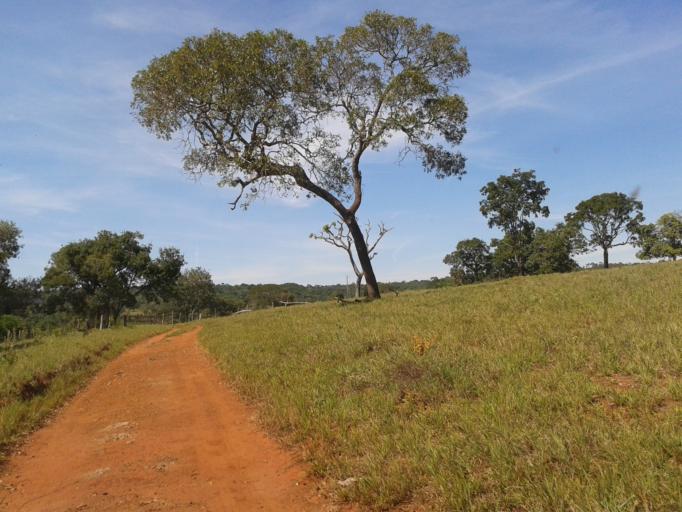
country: BR
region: Minas Gerais
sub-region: Campina Verde
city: Campina Verde
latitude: -19.4353
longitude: -49.6866
